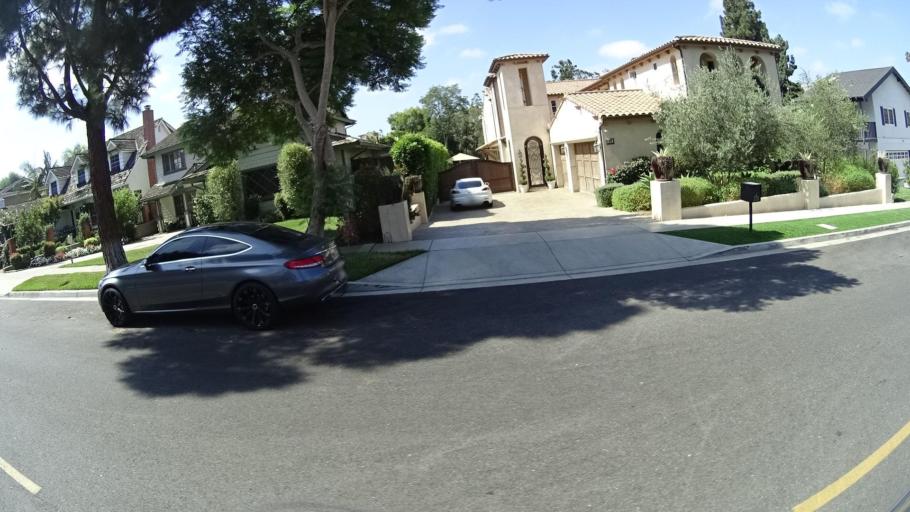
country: US
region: California
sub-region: Orange County
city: Costa Mesa
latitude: 33.6509
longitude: -117.8934
